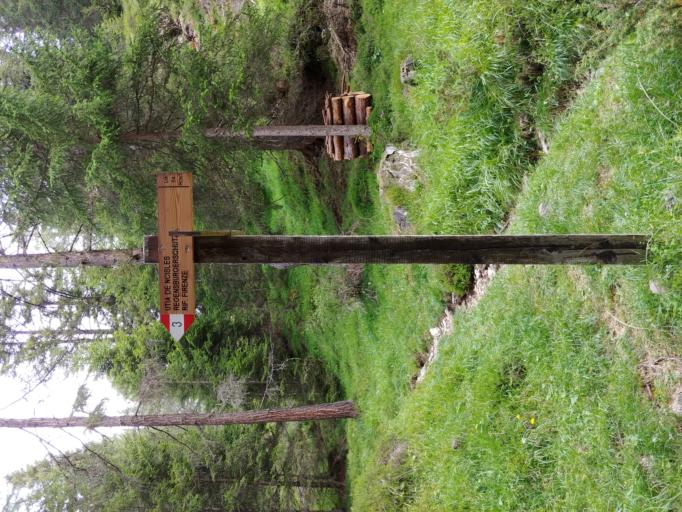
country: IT
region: Trentino-Alto Adige
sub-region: Bolzano
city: Selva
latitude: 46.5645
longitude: 11.7549
